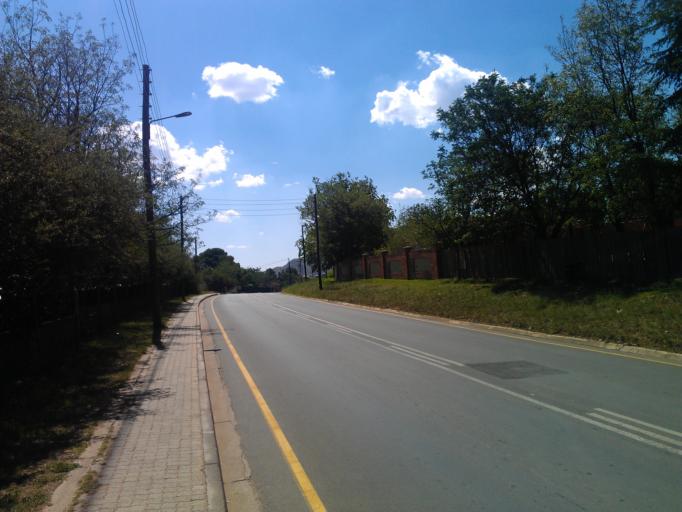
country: LS
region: Maseru
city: Maseru
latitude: -29.3078
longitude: 27.4757
